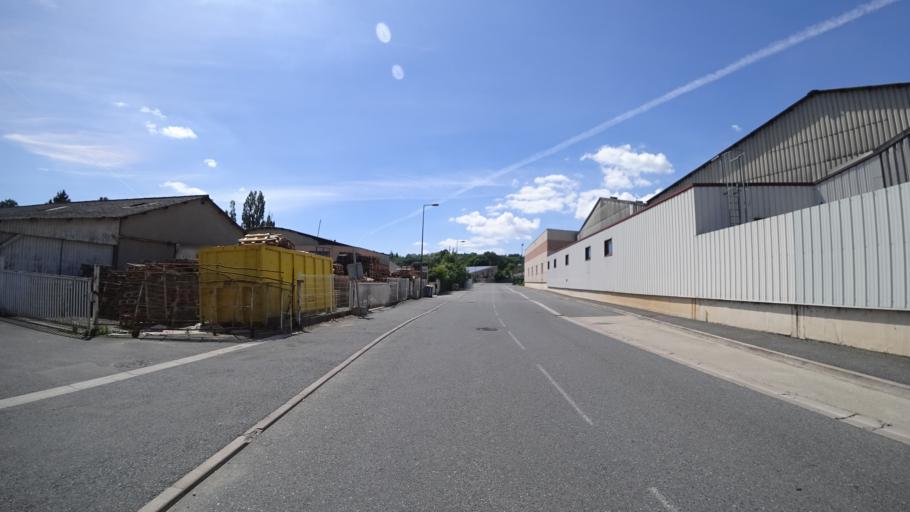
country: FR
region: Midi-Pyrenees
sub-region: Departement de l'Aveyron
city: Le Monastere
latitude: 44.3586
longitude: 2.5968
